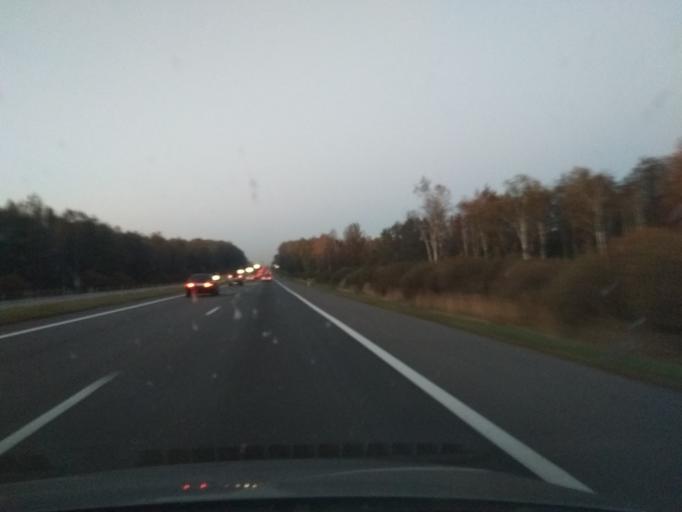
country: BY
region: Minsk
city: Enyerhyetykaw
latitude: 53.6286
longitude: 27.0585
